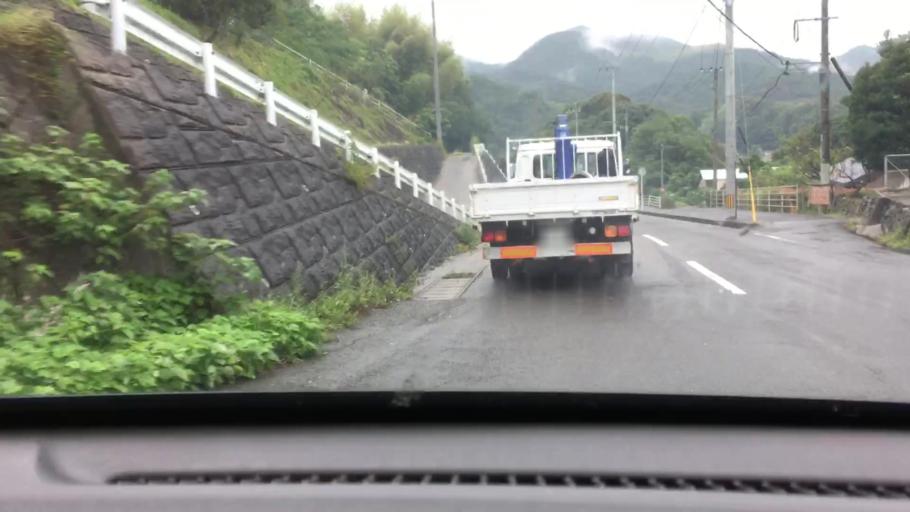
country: JP
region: Nagasaki
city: Togitsu
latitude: 32.8567
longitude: 129.7797
